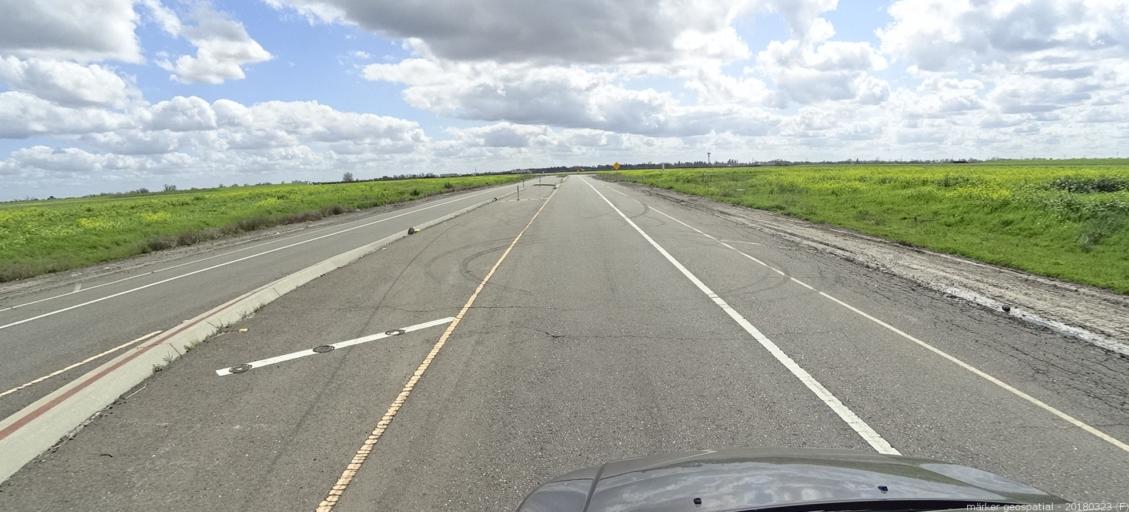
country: US
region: California
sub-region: Yolo County
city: West Sacramento
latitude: 38.6768
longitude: -121.5673
